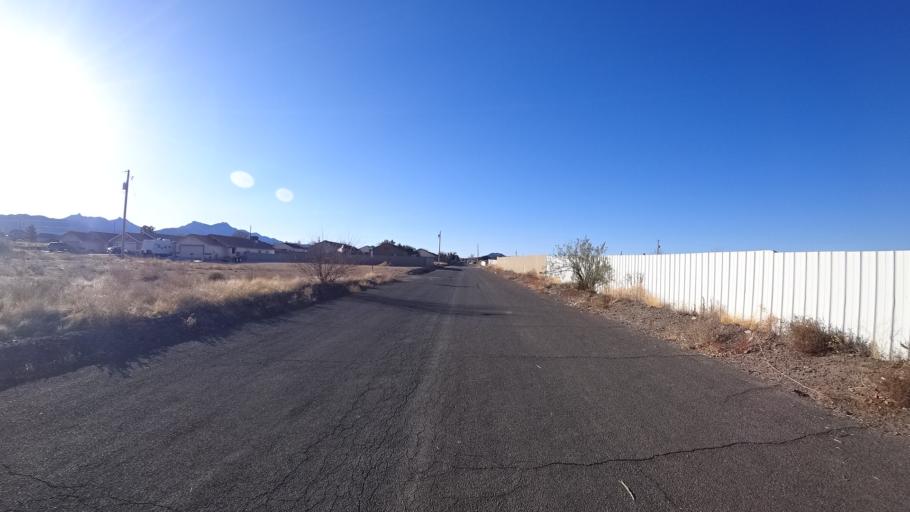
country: US
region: Arizona
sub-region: Mohave County
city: Kingman
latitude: 35.2052
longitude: -114.0158
